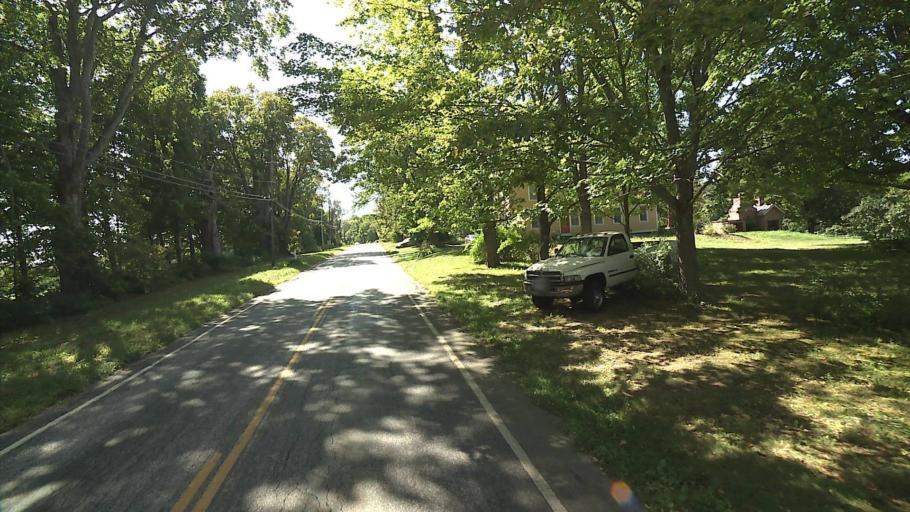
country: US
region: Connecticut
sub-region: Litchfield County
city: Northwest Harwinton
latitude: 41.7294
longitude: -73.0739
